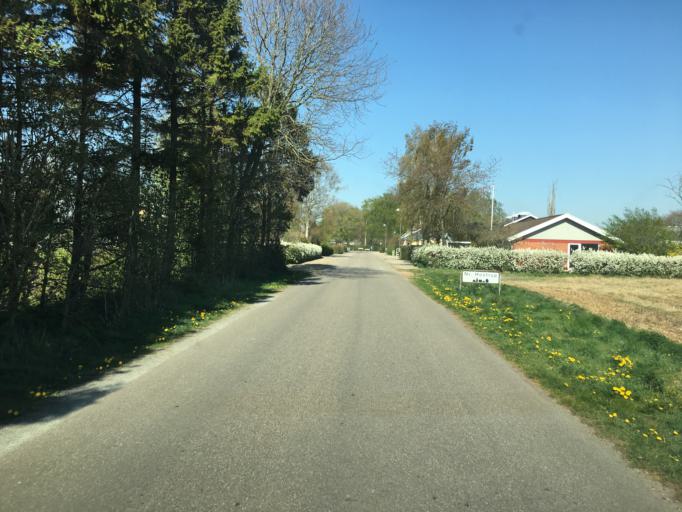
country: DK
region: South Denmark
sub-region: Aabenraa Kommune
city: Rodekro
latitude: 55.0879
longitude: 9.2732
